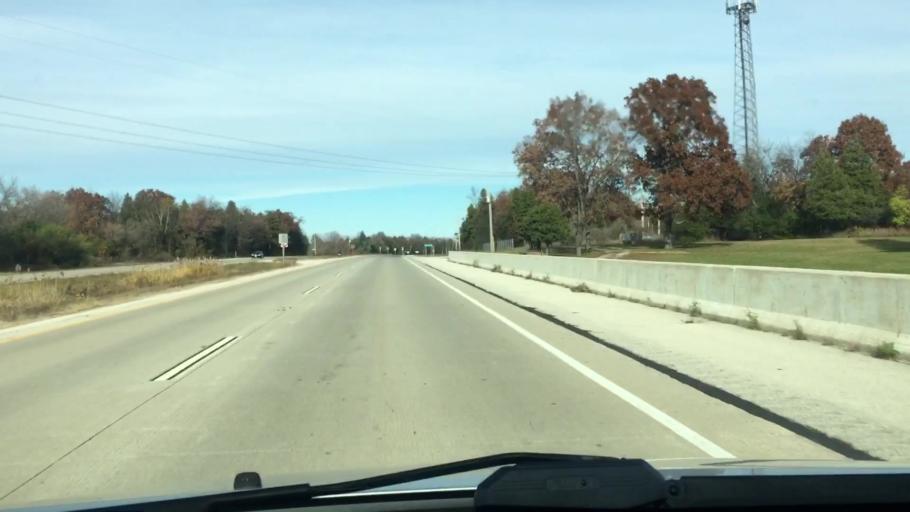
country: US
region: Wisconsin
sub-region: Brown County
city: Bellevue
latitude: 44.5935
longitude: -87.8636
